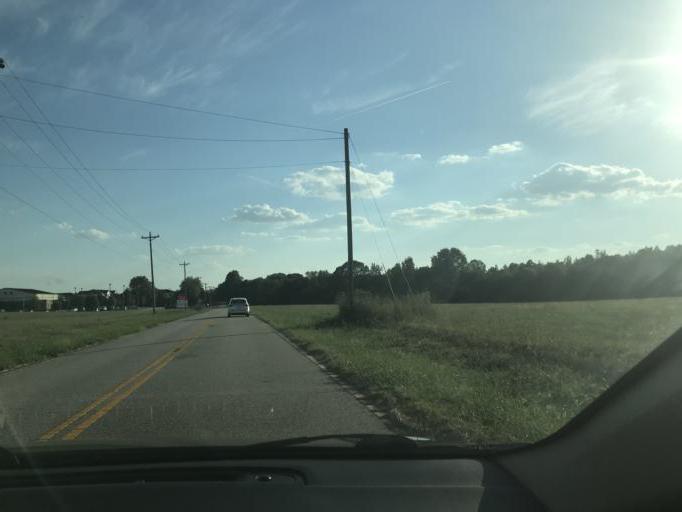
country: US
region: South Carolina
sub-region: Cherokee County
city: Gaffney
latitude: 35.1030
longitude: -81.6876
